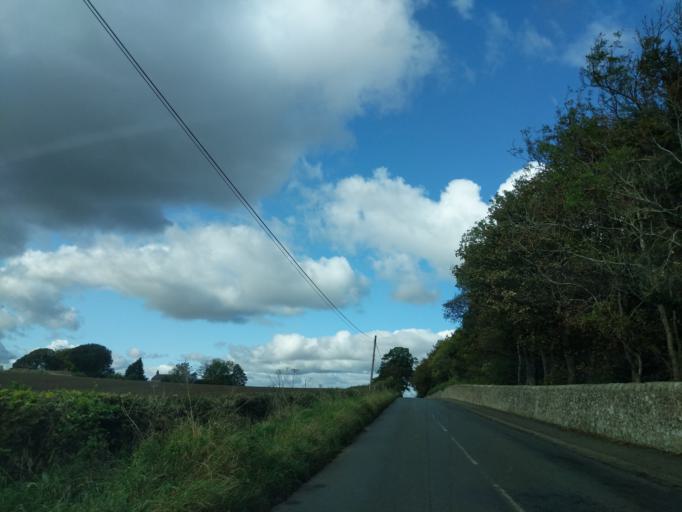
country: GB
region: Scotland
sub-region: Edinburgh
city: Currie
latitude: 55.9026
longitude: -3.3232
